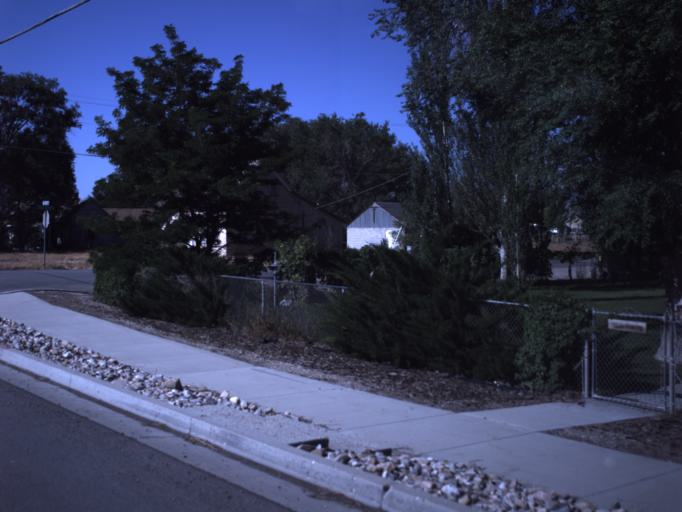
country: US
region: Utah
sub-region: Sanpete County
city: Centerfield
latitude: 39.1308
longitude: -111.8192
